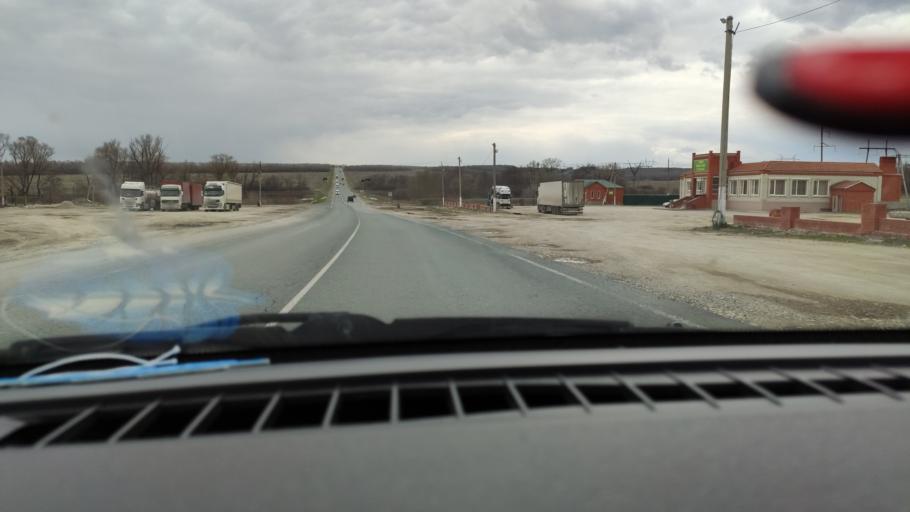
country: RU
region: Saratov
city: Sinodskoye
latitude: 51.9182
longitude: 46.5588
